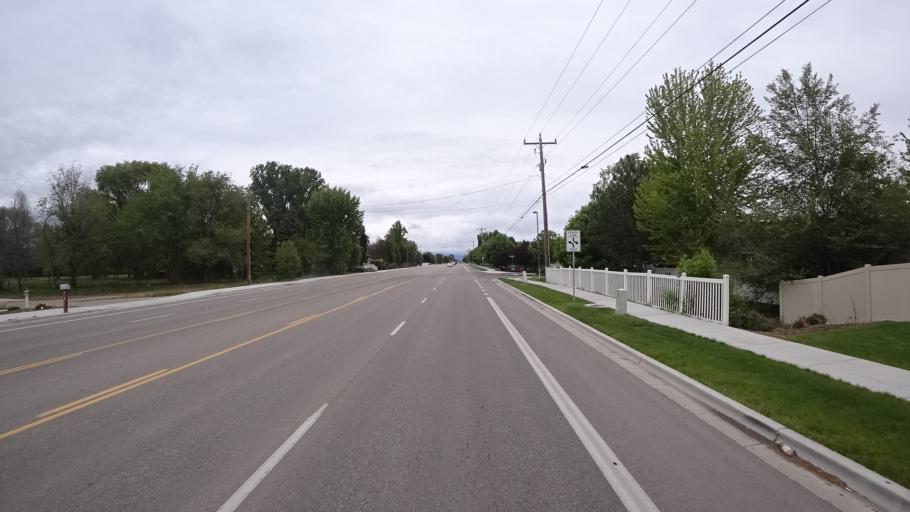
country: US
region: Idaho
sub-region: Ada County
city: Meridian
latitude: 43.6337
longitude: -116.3846
